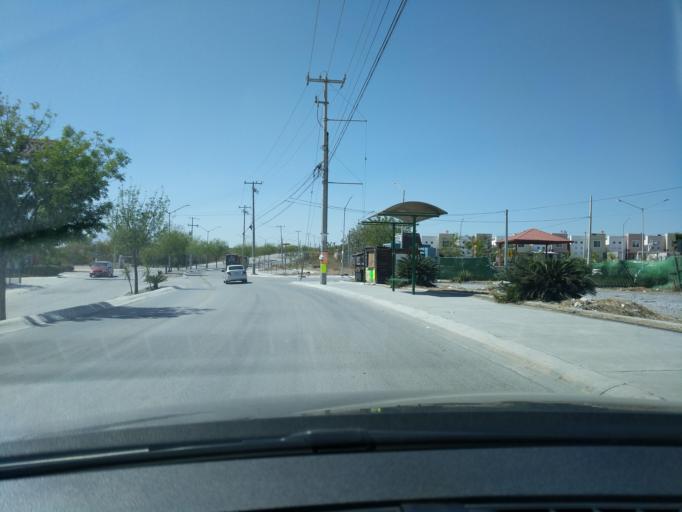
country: MX
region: Nuevo Leon
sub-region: Juarez
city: San Antonio
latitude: 25.6465
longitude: -100.0637
